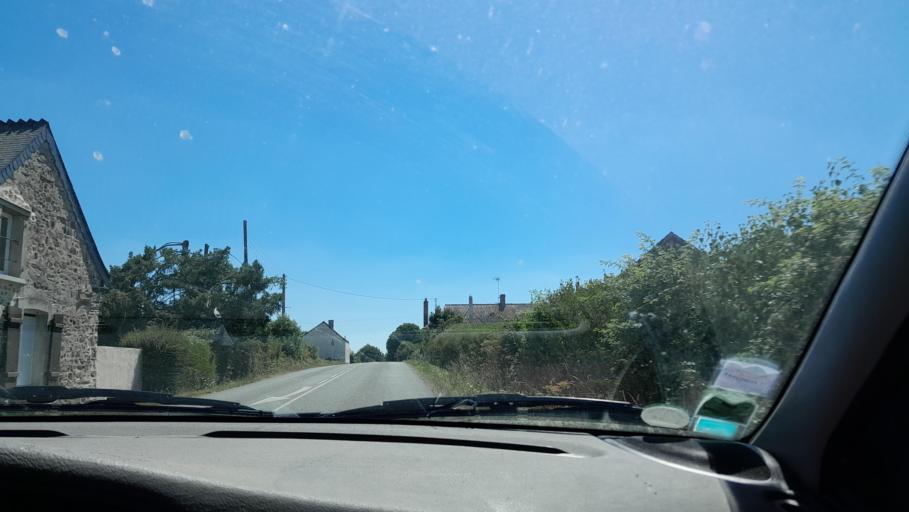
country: FR
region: Pays de la Loire
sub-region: Departement de la Mayenne
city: Congrier
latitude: 47.8688
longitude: -1.1305
